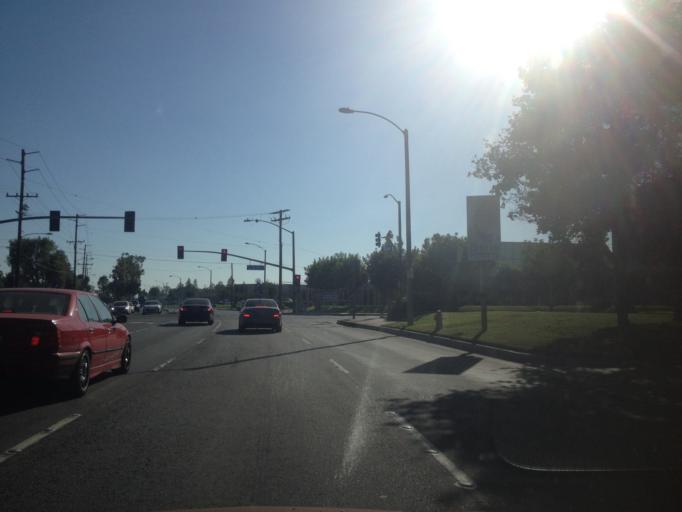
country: US
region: California
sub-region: Orange County
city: Yorba Linda
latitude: 33.8587
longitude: -117.8303
